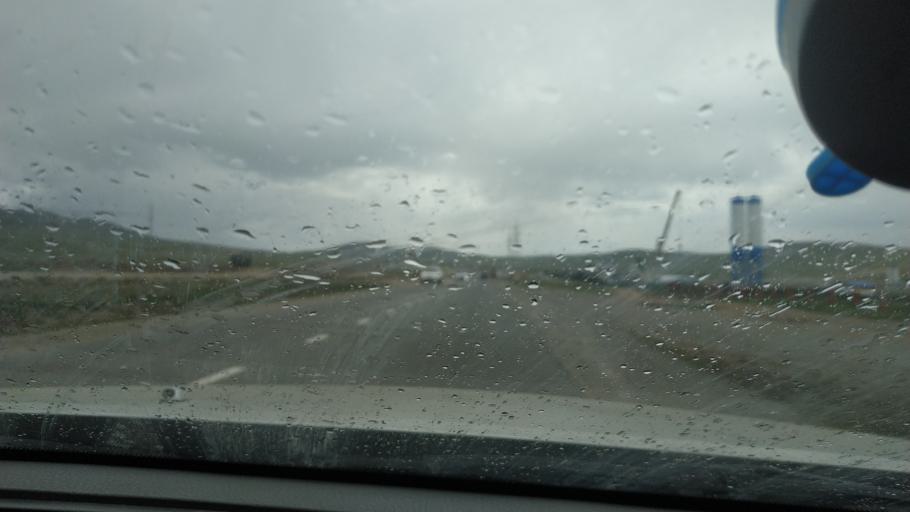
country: MN
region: Ulaanbaatar
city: Ulaanbaatar
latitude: 47.8217
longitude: 106.7622
